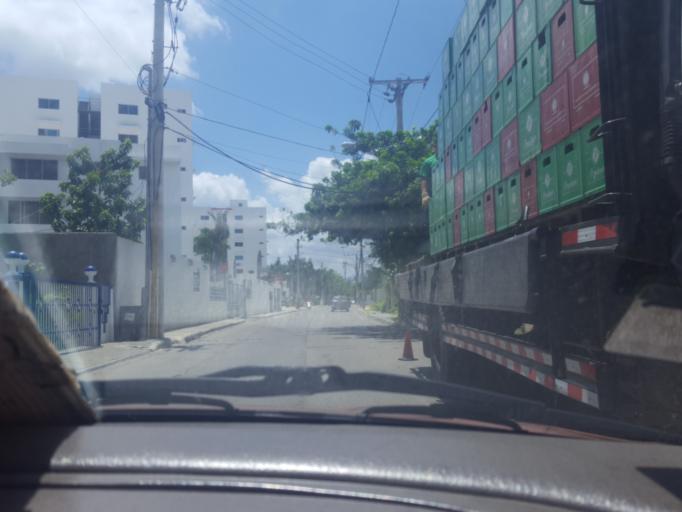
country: DO
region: Santiago
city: Santiago de los Caballeros
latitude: 19.4717
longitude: -70.6653
